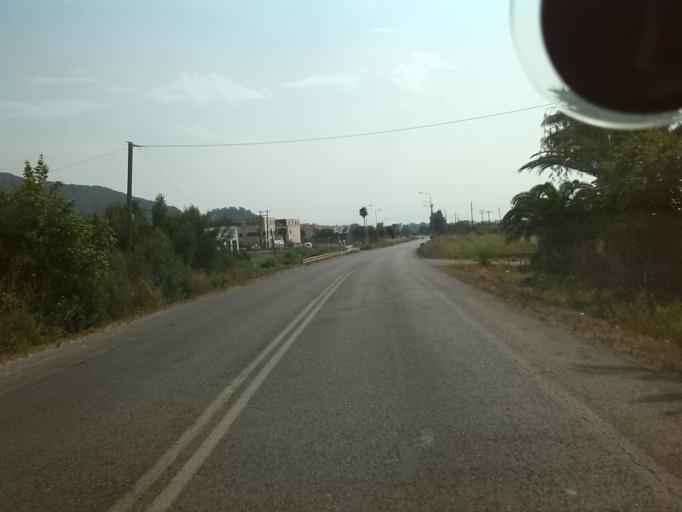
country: GR
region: Peloponnese
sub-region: Nomos Messinias
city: Kyparissia
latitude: 37.2684
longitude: 21.6932
